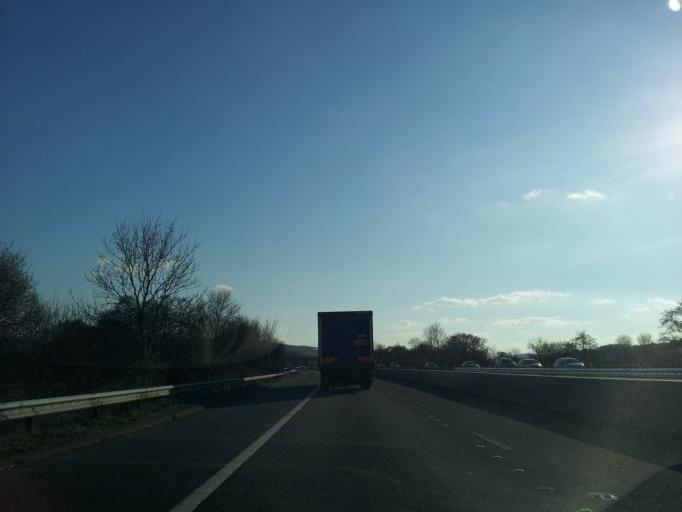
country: GB
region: England
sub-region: Devon
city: Bradninch
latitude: 50.8326
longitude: -3.3972
